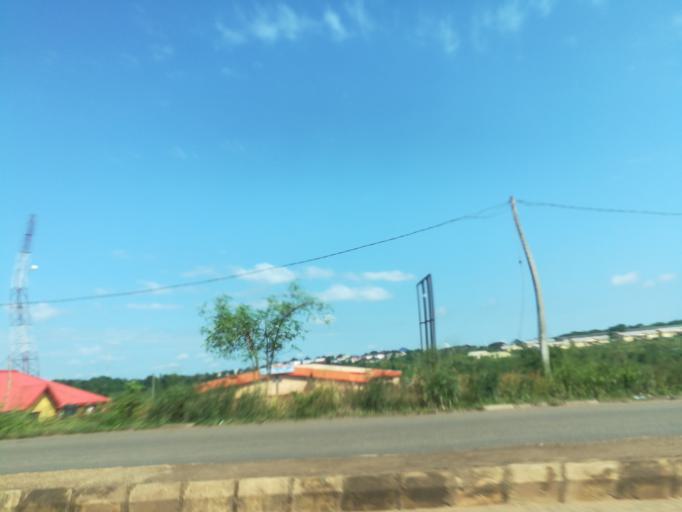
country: NG
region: Oyo
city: Ibadan
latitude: 7.4163
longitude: 3.9615
